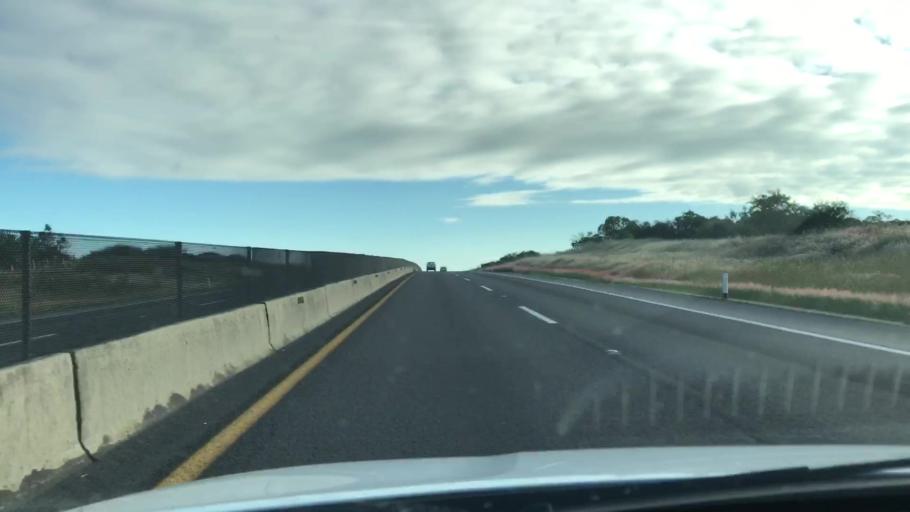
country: MX
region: Jalisco
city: Valle de Guadalupe
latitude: 21.0564
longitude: -102.5234
